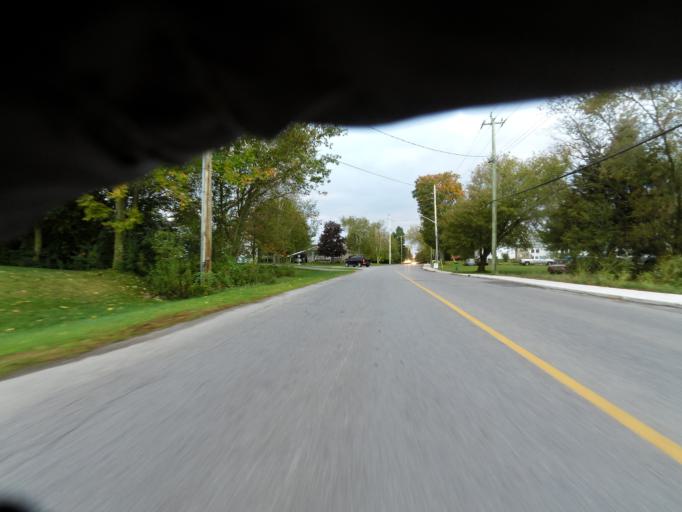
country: CA
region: Ontario
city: Quinte West
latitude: 44.0269
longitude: -77.7253
